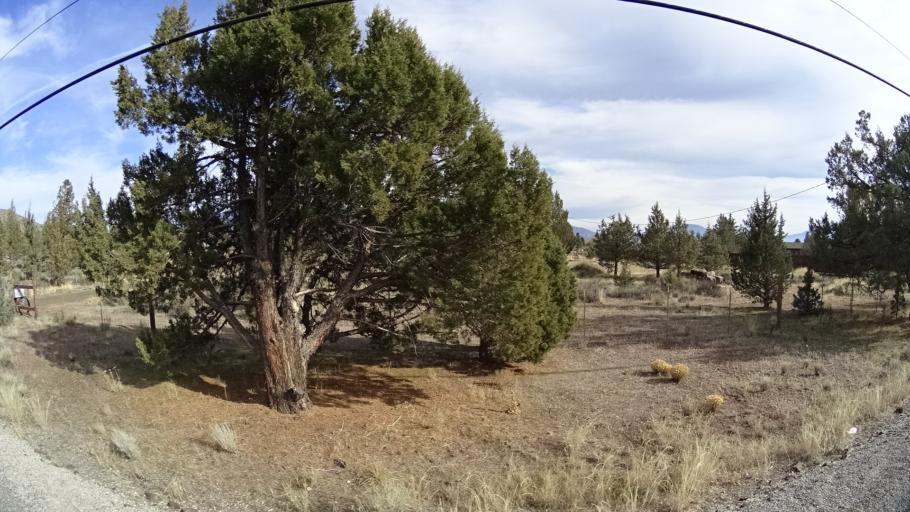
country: US
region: California
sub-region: Siskiyou County
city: Montague
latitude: 41.6517
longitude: -122.3993
